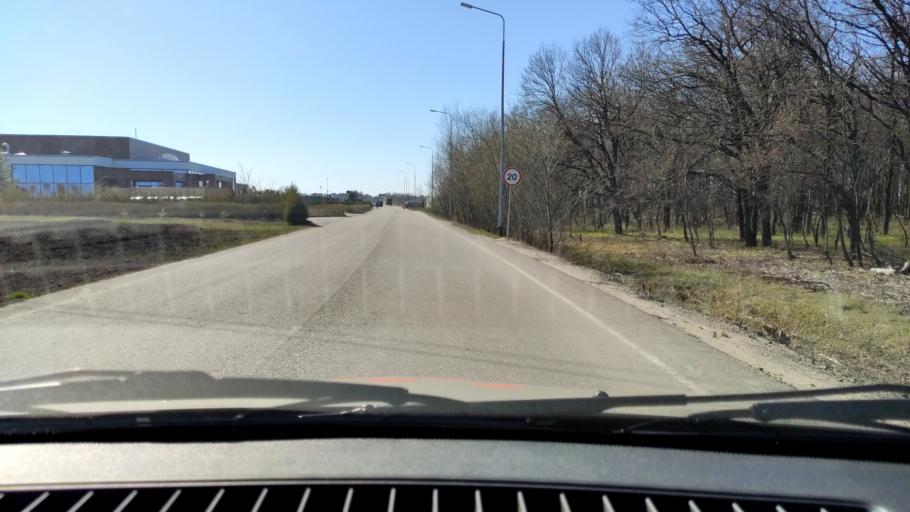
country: RU
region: Voronezj
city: Somovo
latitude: 51.6871
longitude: 39.3409
